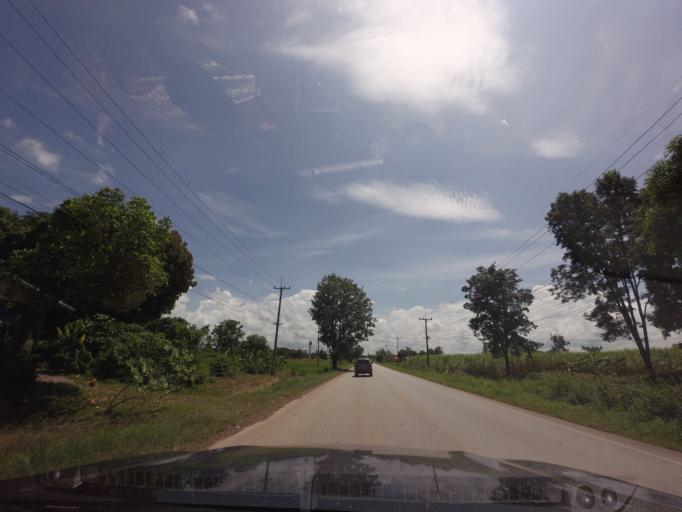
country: TH
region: Changwat Udon Thani
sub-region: Amphoe Ban Phue
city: Ban Phue
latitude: 17.7105
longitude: 102.4187
